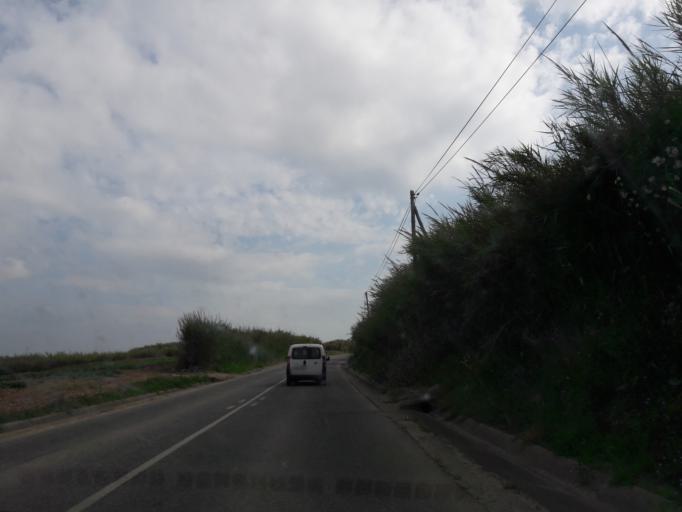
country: PT
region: Leiria
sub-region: Peniche
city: Atouguia da Baleia
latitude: 39.3555
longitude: -9.3195
